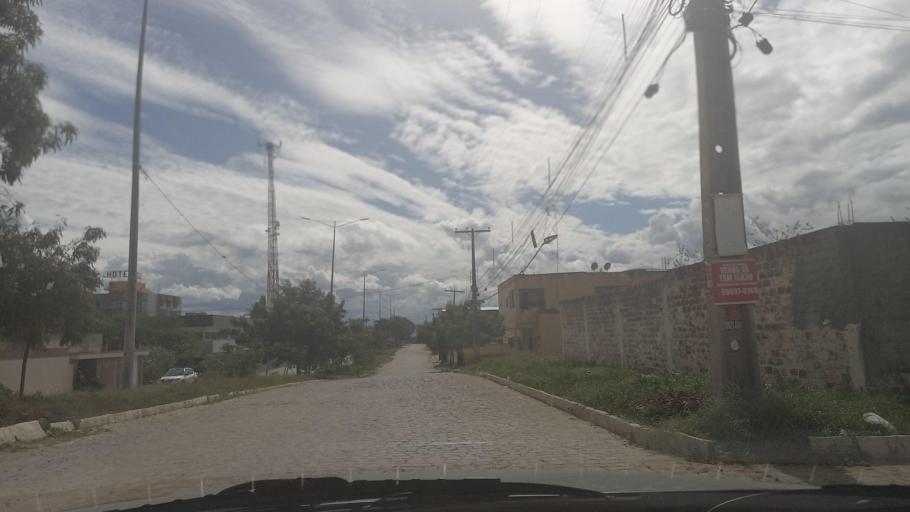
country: BR
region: Pernambuco
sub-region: Caruaru
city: Caruaru
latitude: -8.2927
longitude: -35.9881
